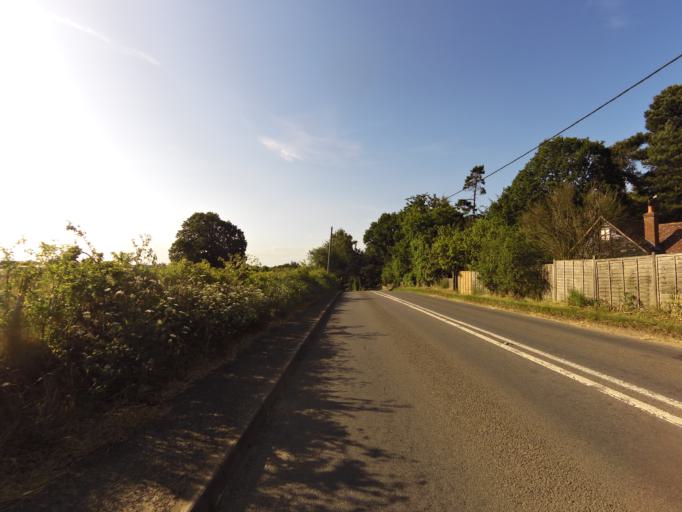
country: GB
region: England
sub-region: Suffolk
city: Woodbridge
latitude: 52.0977
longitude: 1.3484
